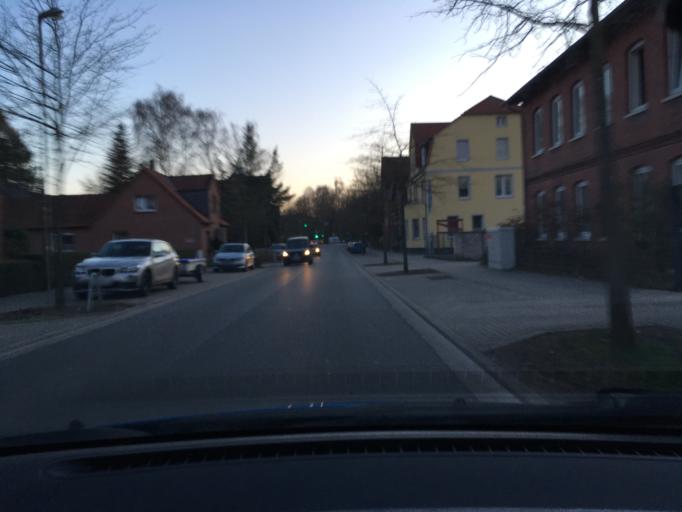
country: DE
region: Lower Saxony
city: Uelzen
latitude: 52.9750
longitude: 10.5668
